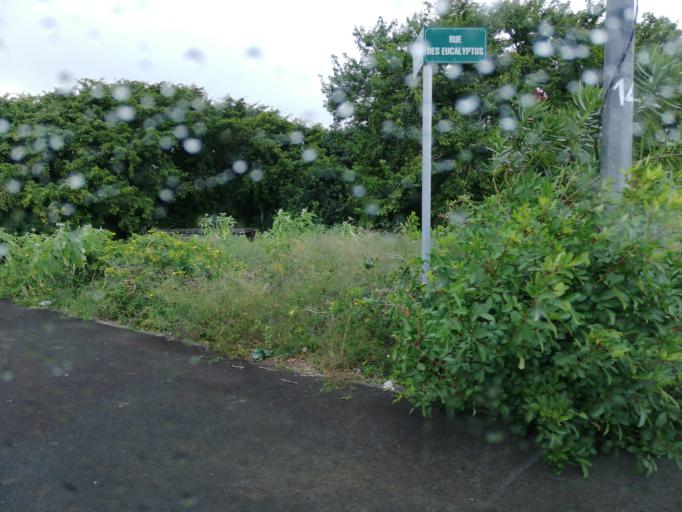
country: MU
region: Plaines Wilhems
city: Ebene
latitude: -20.2487
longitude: 57.4869
